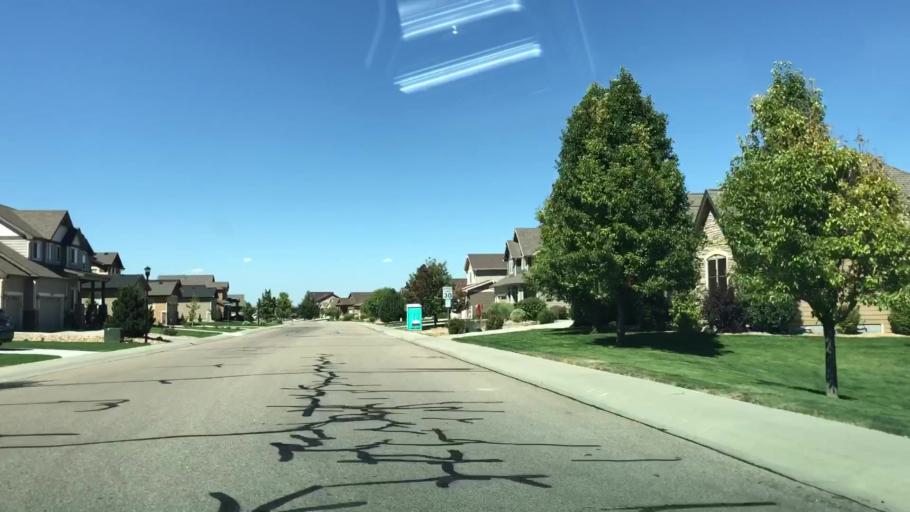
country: US
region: Colorado
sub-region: Weld County
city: Windsor
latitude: 40.4522
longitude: -104.9485
